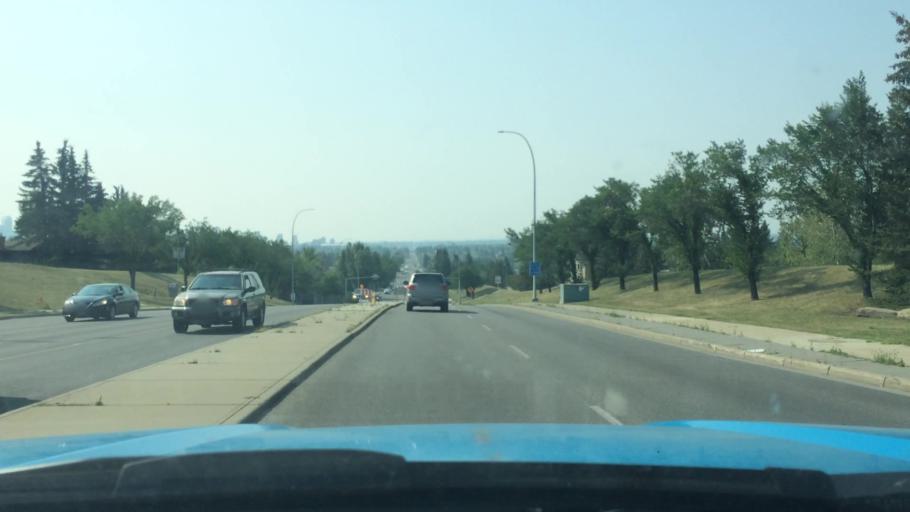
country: CA
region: Alberta
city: Calgary
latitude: 51.0894
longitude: -114.0948
